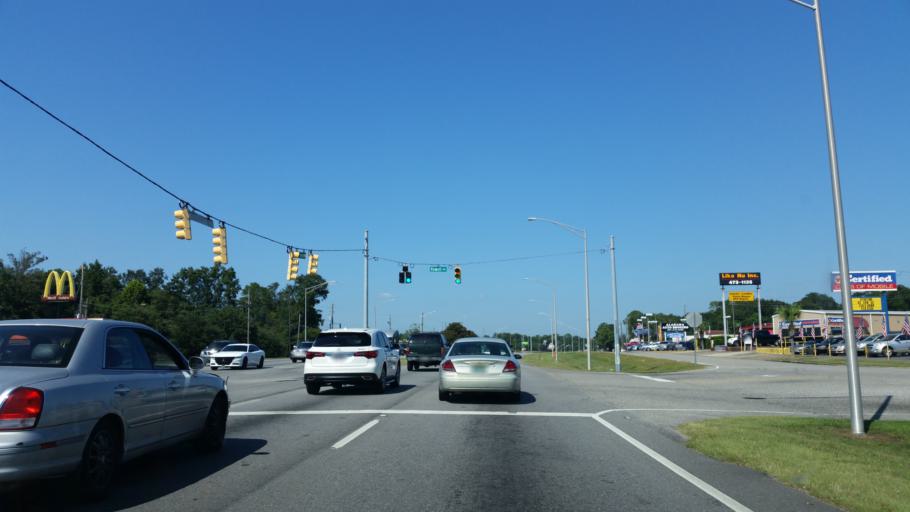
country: US
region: Alabama
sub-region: Mobile County
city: Mobile
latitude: 30.6649
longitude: -88.1062
